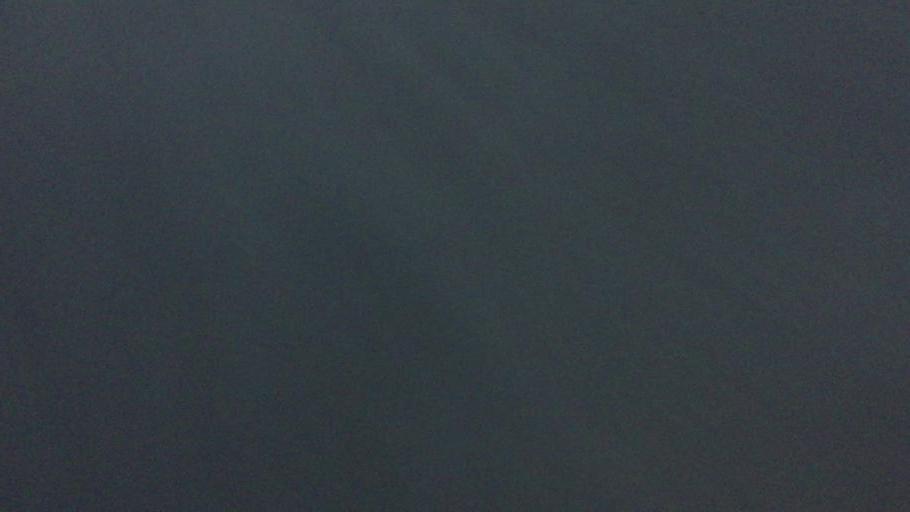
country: US
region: Georgia
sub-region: Carroll County
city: Carrollton
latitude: 33.6076
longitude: -85.0181
